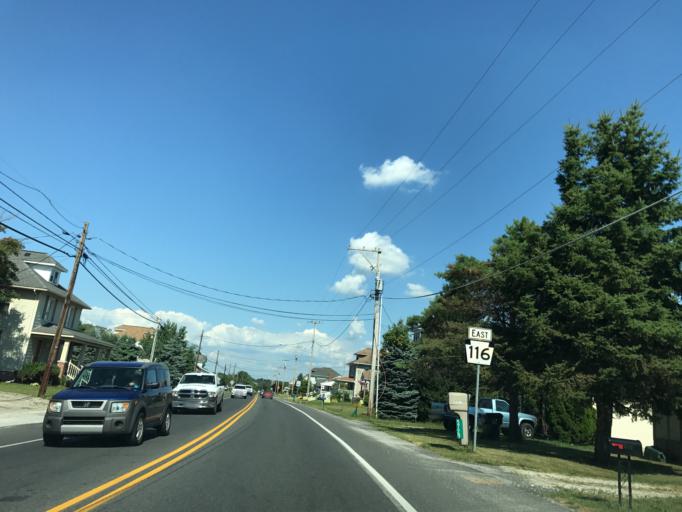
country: US
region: Pennsylvania
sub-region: Adams County
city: McSherrystown
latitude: 39.7967
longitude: -77.0400
